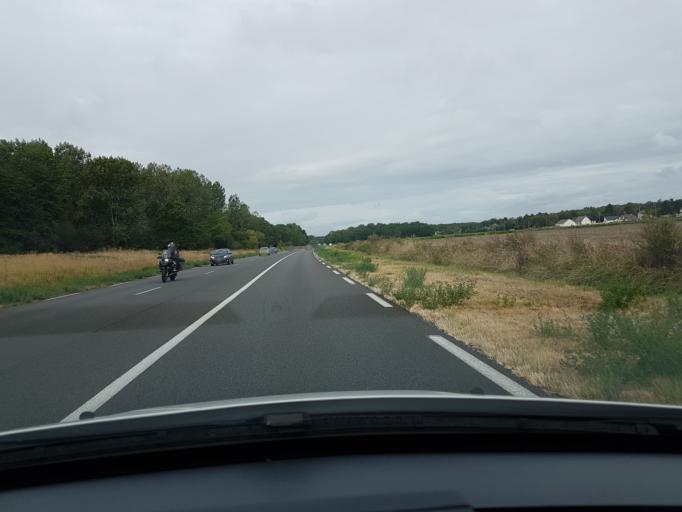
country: FR
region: Centre
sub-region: Departement d'Indre-et-Loire
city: Azay-sur-Cher
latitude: 47.3608
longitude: 0.8718
